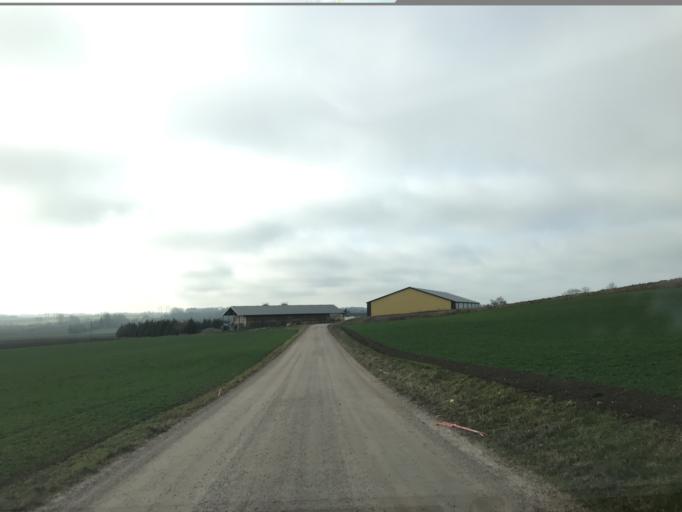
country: SE
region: Skane
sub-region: Svalovs Kommun
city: Teckomatorp
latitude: 55.8285
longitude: 13.0729
